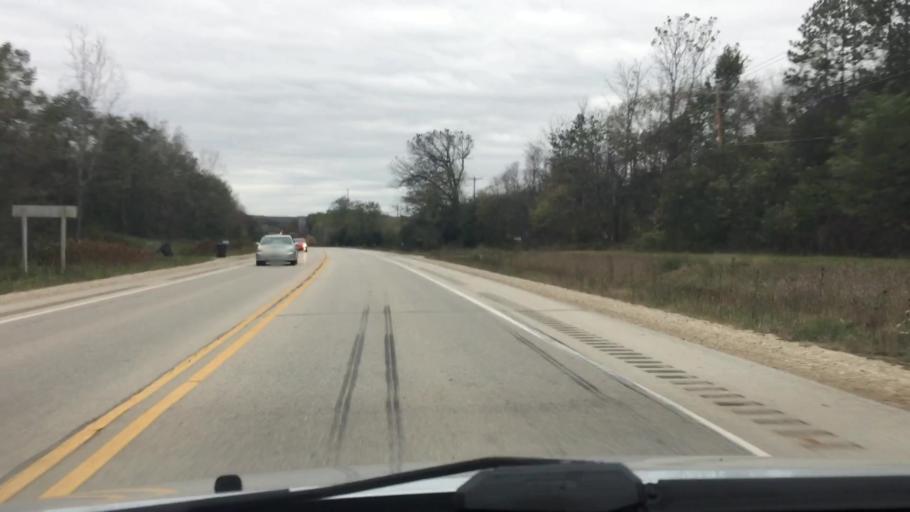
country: US
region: Wisconsin
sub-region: Waukesha County
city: Wales
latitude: 42.9718
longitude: -88.3073
